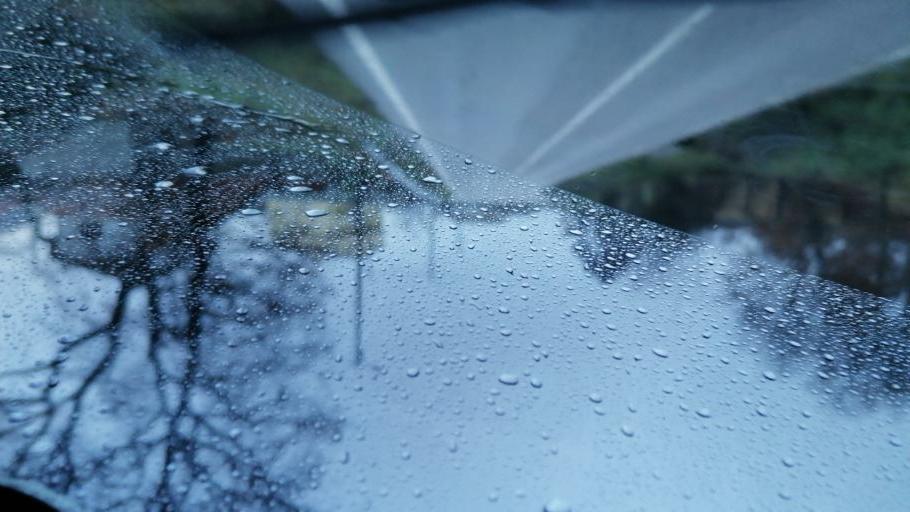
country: PT
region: Vila Real
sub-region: Murca
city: Murca
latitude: 41.4388
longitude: -7.5497
